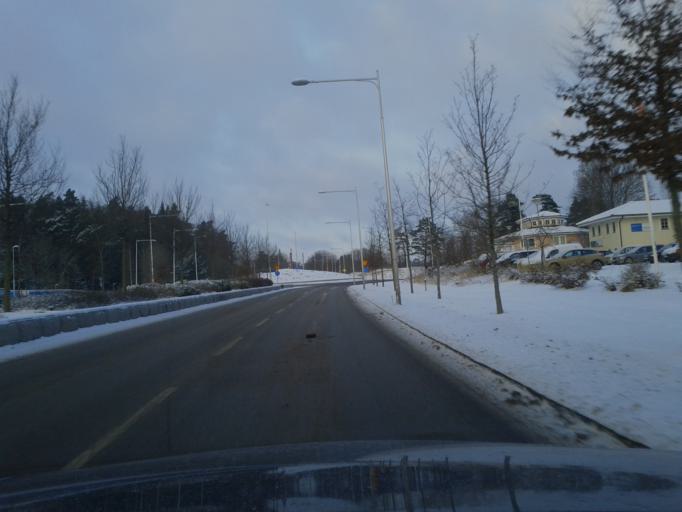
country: SE
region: Stockholm
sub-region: Taby Kommun
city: Taby
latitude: 59.4522
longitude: 18.0869
